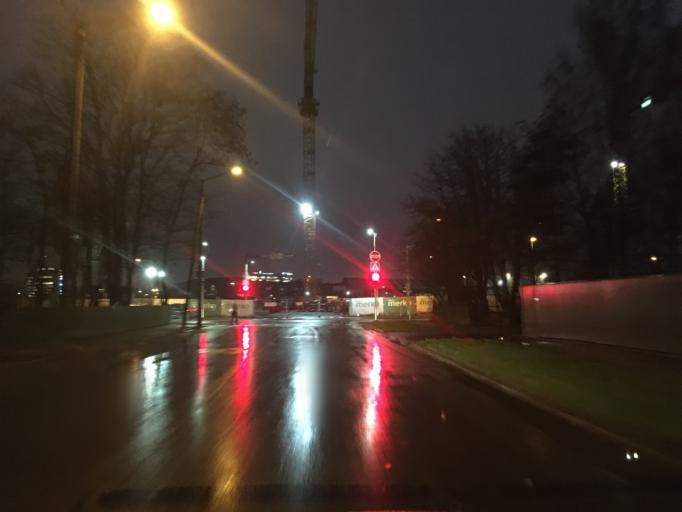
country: EE
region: Harju
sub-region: Tallinna linn
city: Tallinn
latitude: 59.4208
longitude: 24.7518
